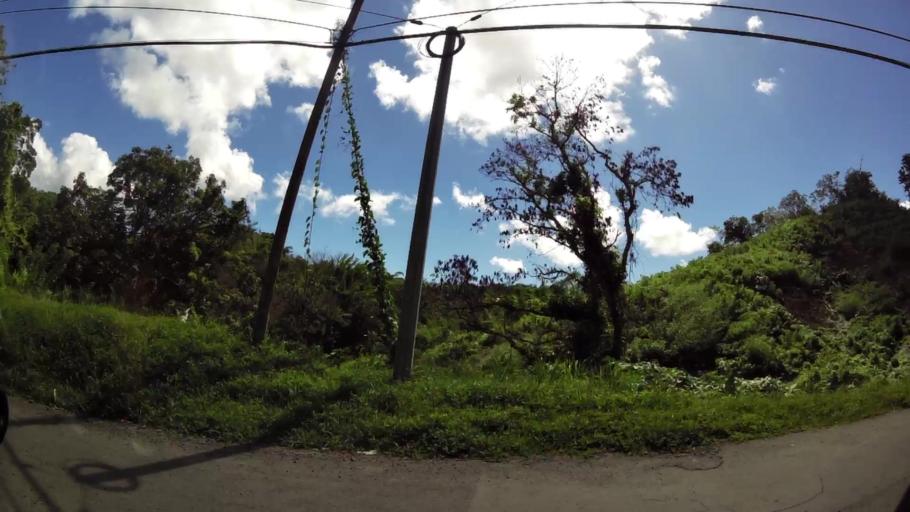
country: TT
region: Tobago
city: Scarborough
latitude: 11.2240
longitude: -60.7537
